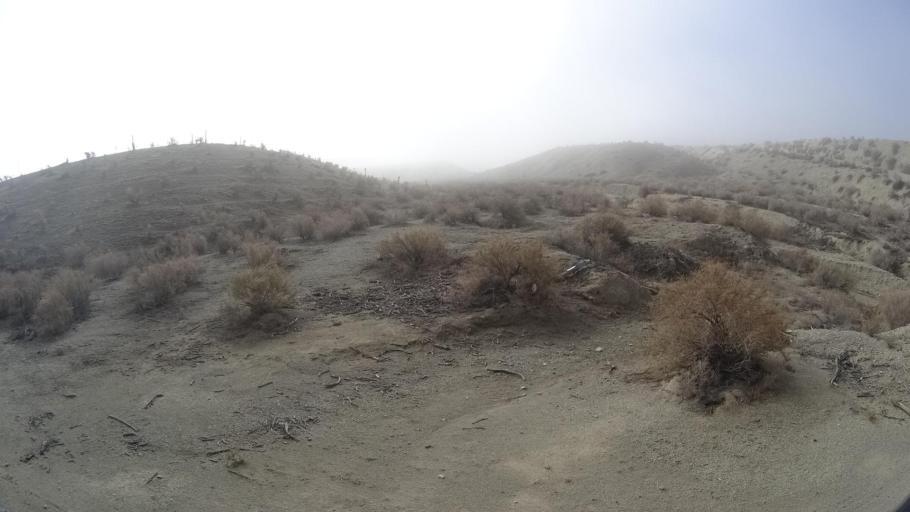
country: US
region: California
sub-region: Kern County
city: Maricopa
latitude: 35.0218
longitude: -119.4472
